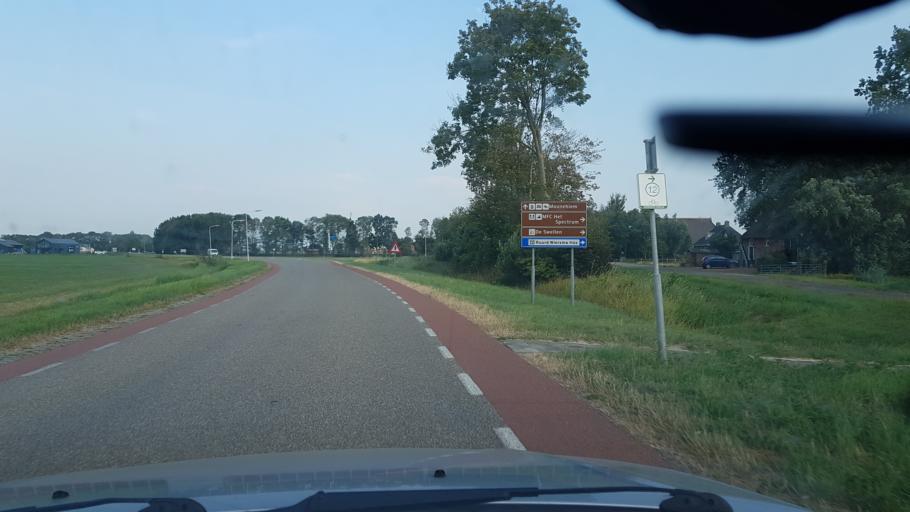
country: NL
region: Friesland
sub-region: Gemeente Ferwerderadiel
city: Burdaard
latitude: 53.3003
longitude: 5.8758
